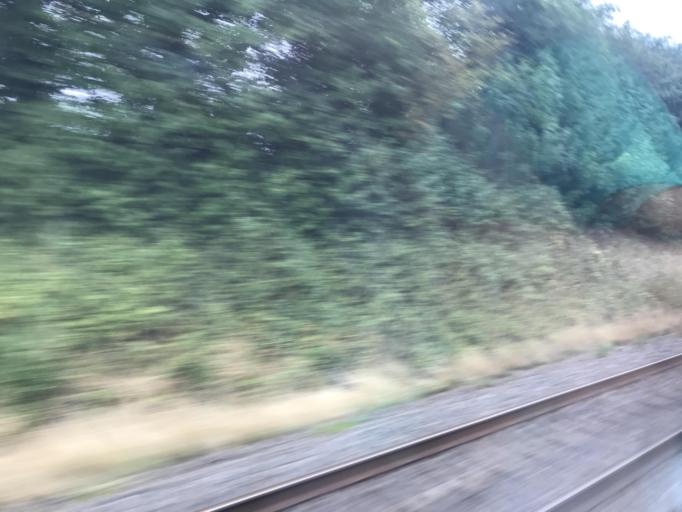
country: DE
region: North Rhine-Westphalia
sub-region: Regierungsbezirk Koln
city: Eschweiler
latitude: 50.8071
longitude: 6.2922
